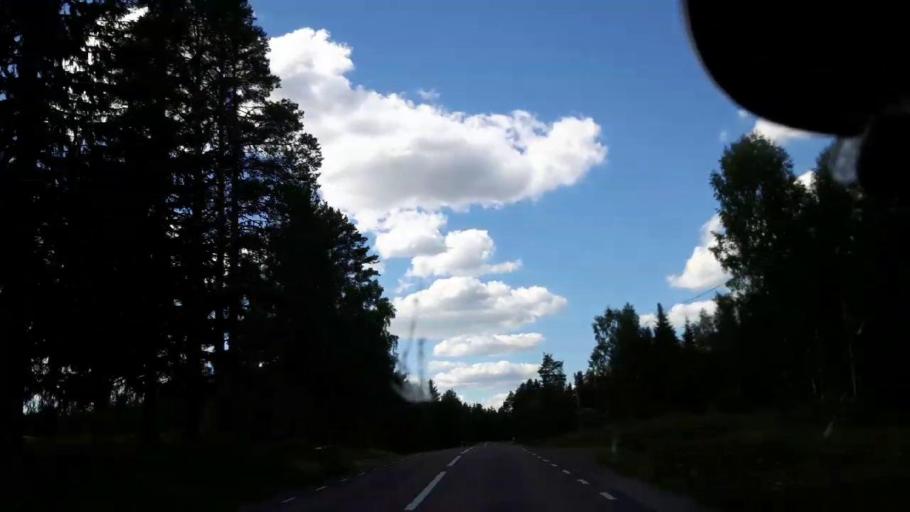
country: SE
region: Jaemtland
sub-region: Ragunda Kommun
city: Hammarstrand
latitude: 63.0189
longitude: 16.5796
